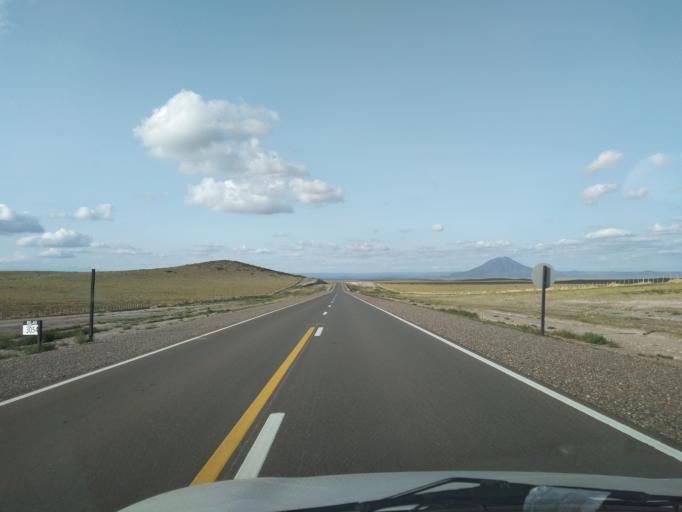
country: AR
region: Mendoza
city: Malargue
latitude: -34.8078
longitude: -69.2442
